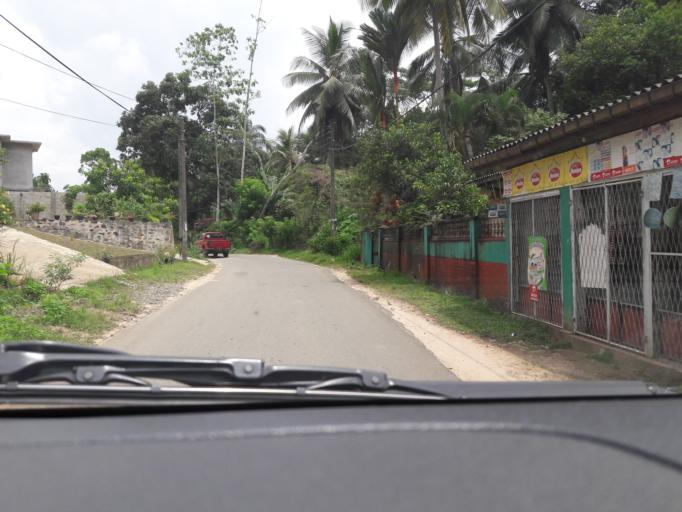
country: LK
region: Southern
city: Galle
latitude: 6.1743
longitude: 80.2871
